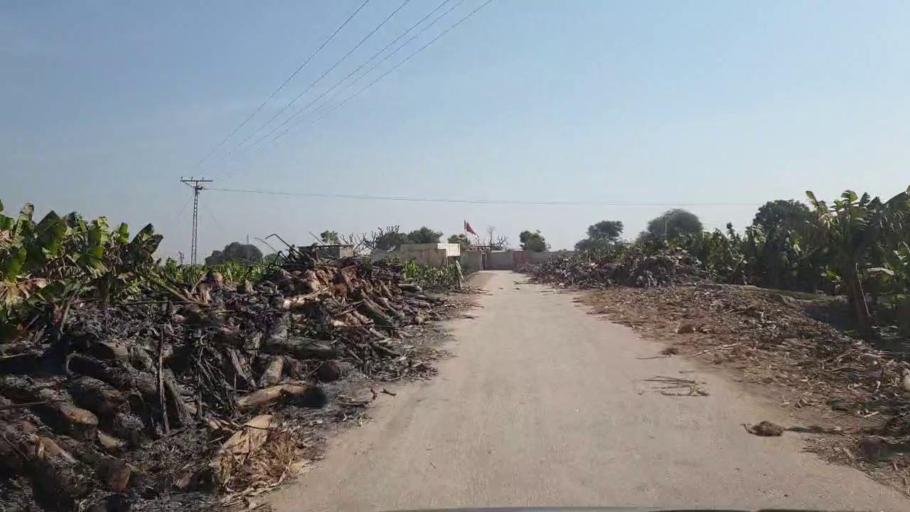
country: PK
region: Sindh
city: Chambar
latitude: 25.3822
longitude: 68.7779
